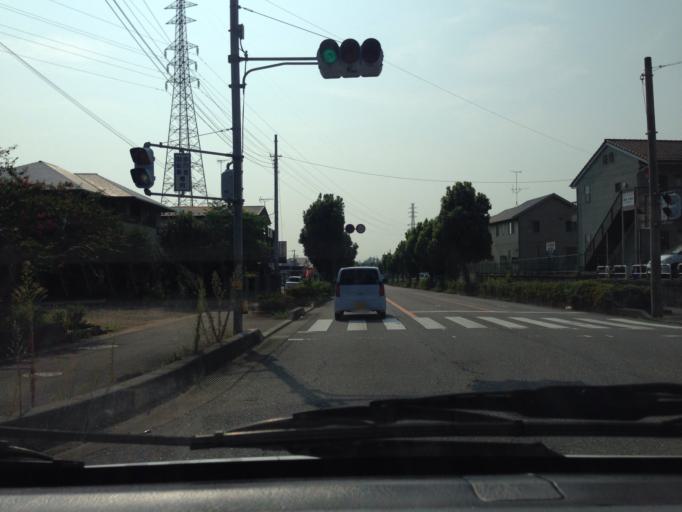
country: JP
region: Ibaraki
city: Ami
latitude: 36.0405
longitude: 140.2198
